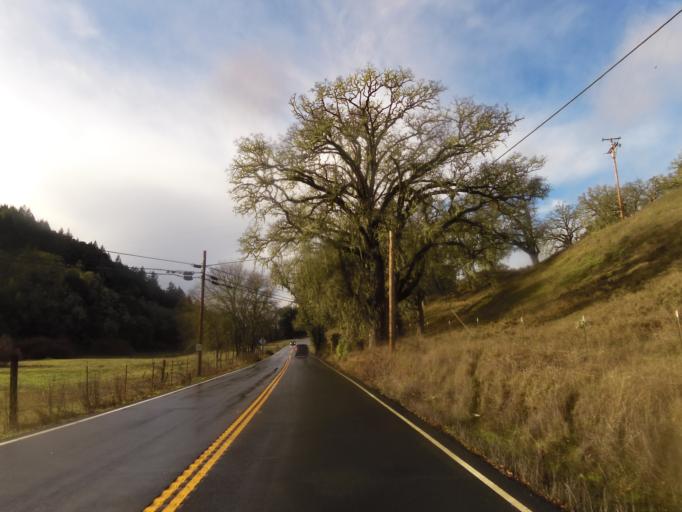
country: US
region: California
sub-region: Sonoma County
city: Cloverdale
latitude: 38.8817
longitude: -123.1378
